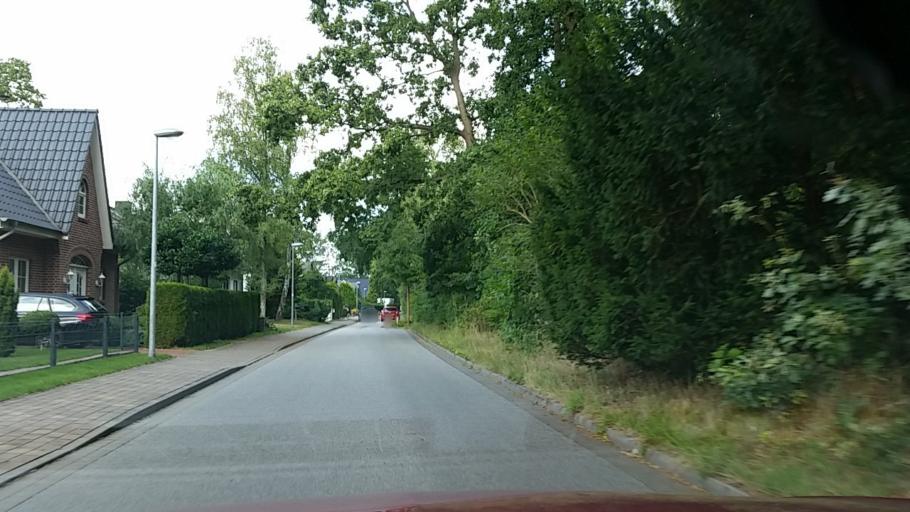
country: DE
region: Schleswig-Holstein
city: Wedel
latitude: 53.5981
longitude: 9.7293
